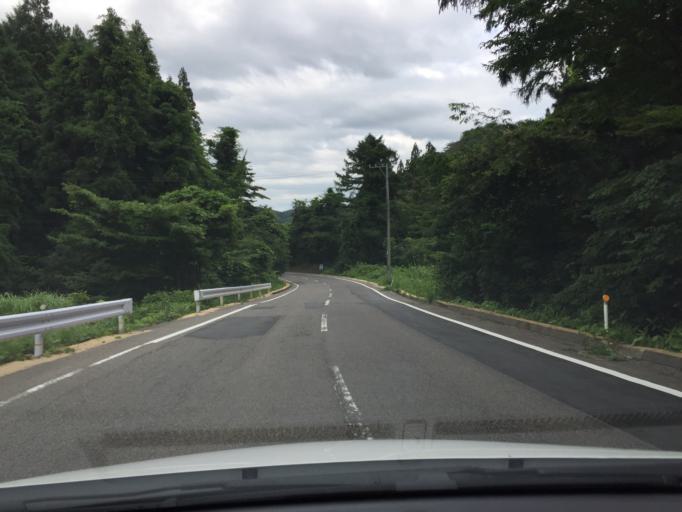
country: JP
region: Fukushima
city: Sukagawa
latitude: 37.1827
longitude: 140.1806
